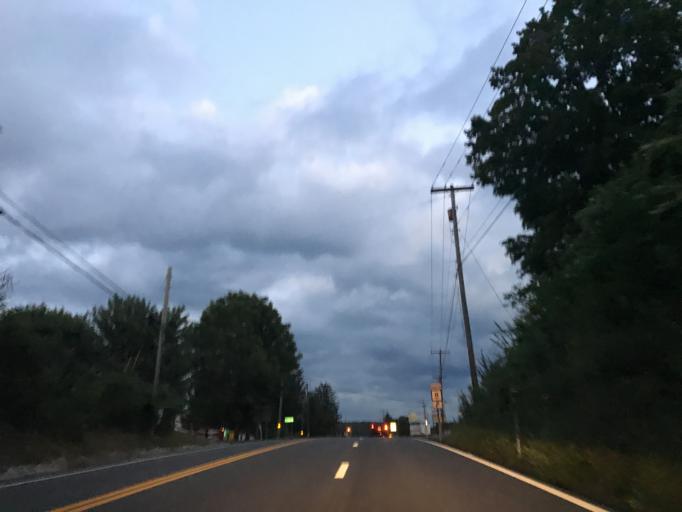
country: US
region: West Virginia
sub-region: Hancock County
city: Chester
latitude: 40.5987
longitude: -80.5417
